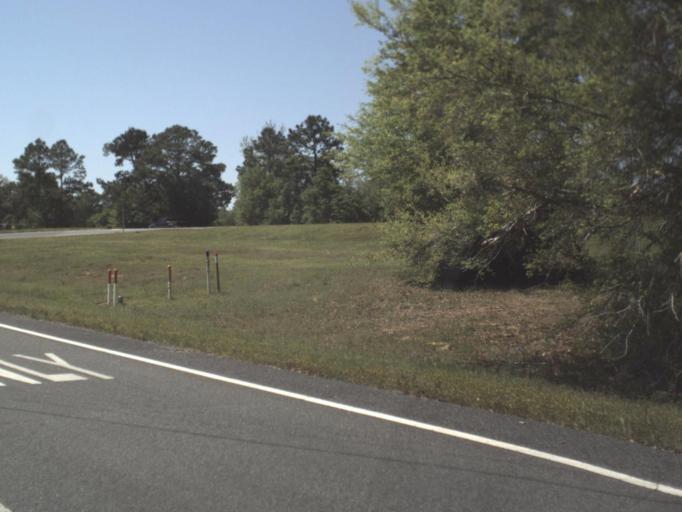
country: US
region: Florida
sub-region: Escambia County
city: Cantonment
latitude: 30.5347
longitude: -87.4065
